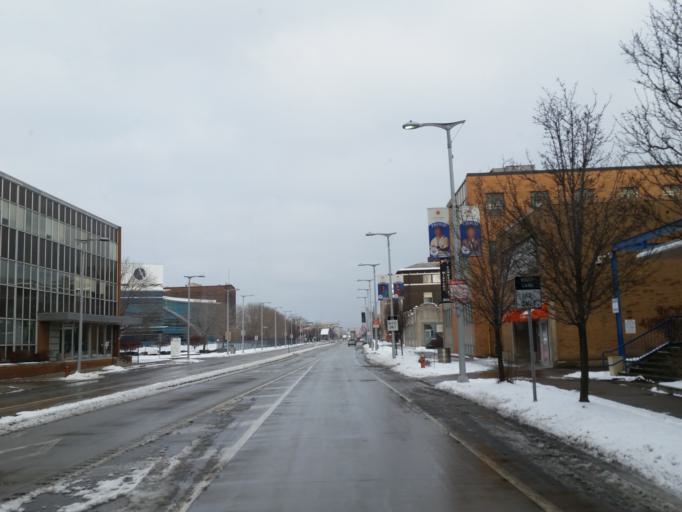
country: US
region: Ohio
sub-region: Cuyahoga County
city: Cleveland
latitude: 41.5026
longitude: -81.6664
